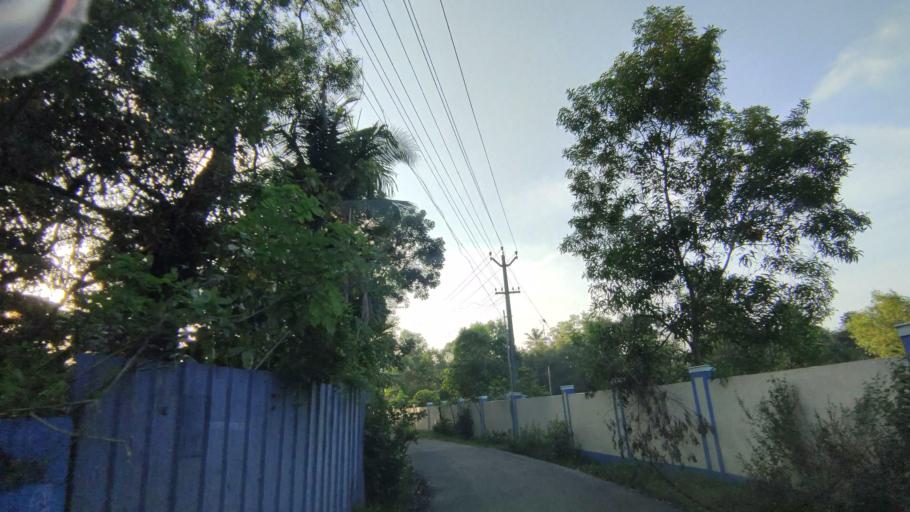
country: IN
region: Kerala
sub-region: Alappuzha
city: Shertallai
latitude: 9.6525
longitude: 76.3502
